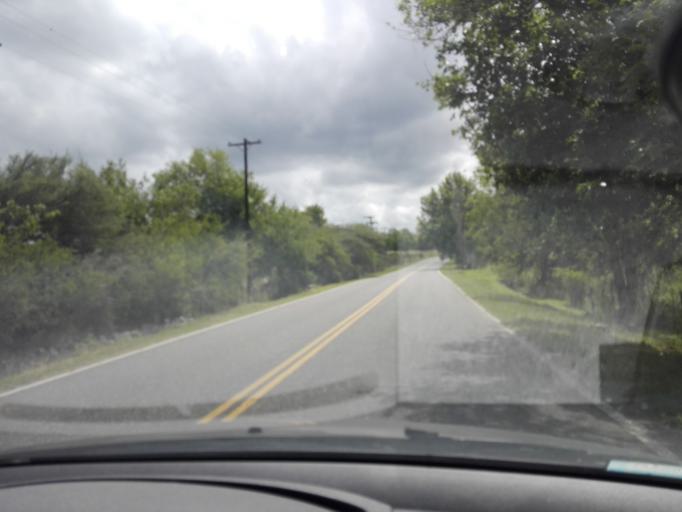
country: AR
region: Cordoba
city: Alta Gracia
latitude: -31.5875
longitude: -64.4717
